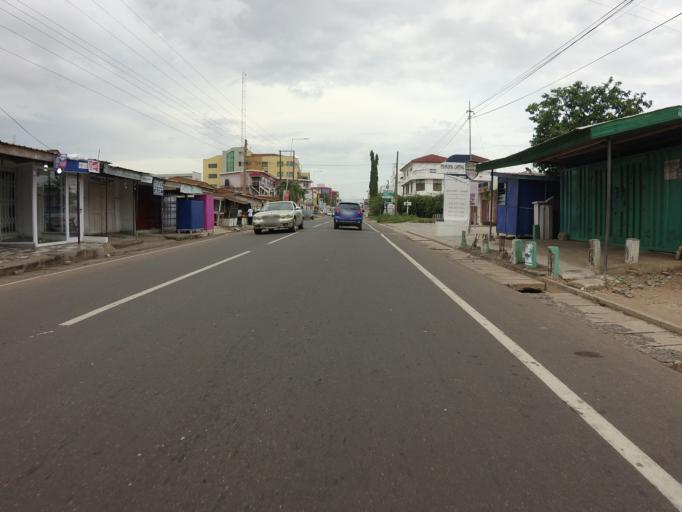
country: GH
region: Greater Accra
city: Dome
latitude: 5.6099
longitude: -0.2052
